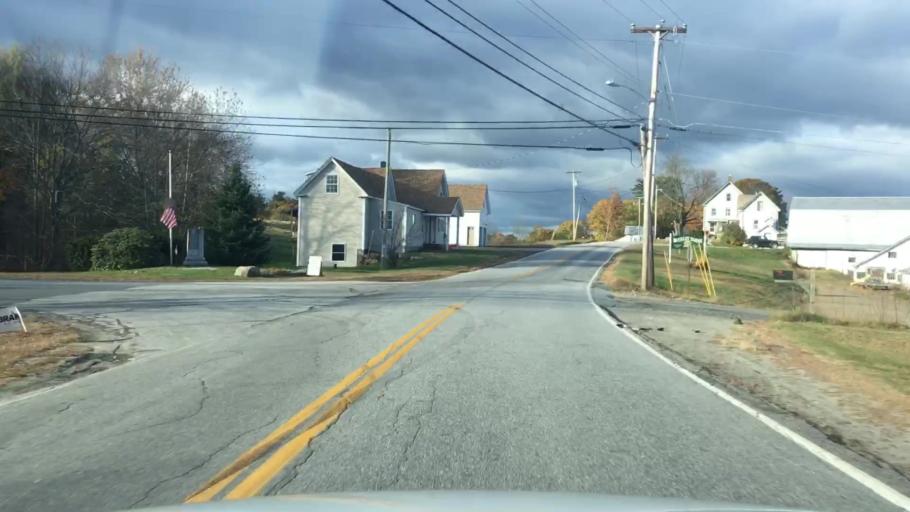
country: US
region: Maine
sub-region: Androscoggin County
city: Leeds
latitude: 44.3033
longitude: -70.1191
